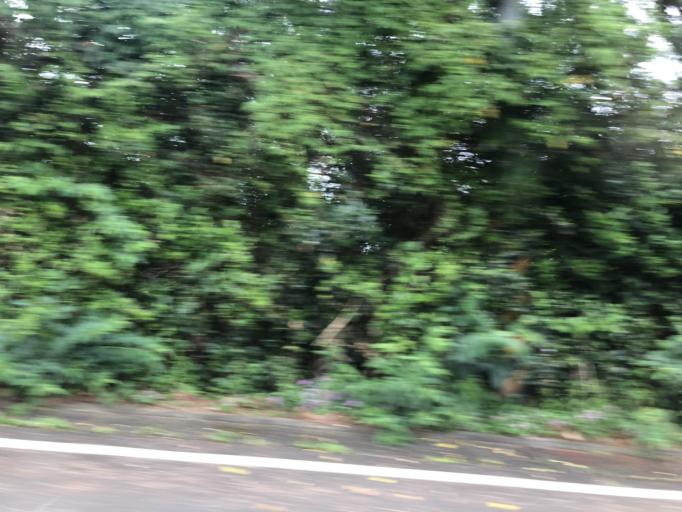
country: TW
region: Taiwan
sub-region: Keelung
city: Keelung
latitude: 25.2189
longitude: 121.6478
